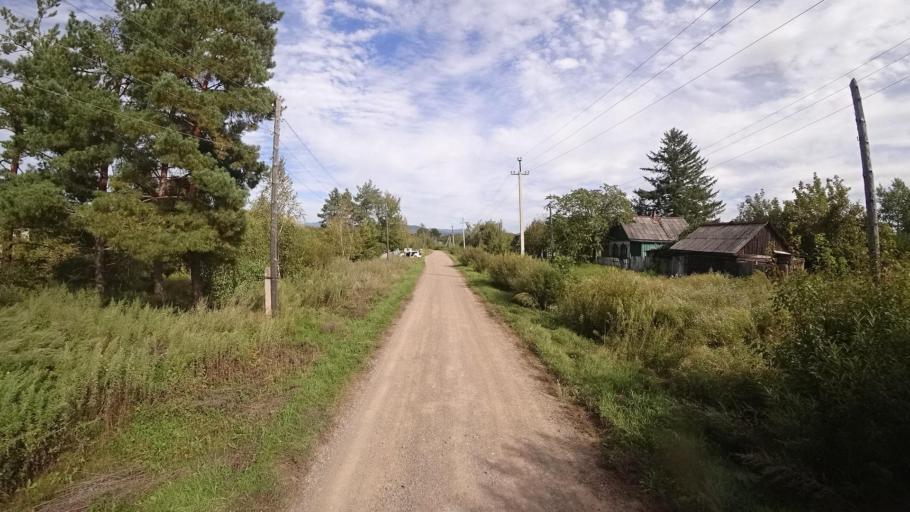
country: RU
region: Primorskiy
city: Dostoyevka
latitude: 44.3286
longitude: 133.4817
